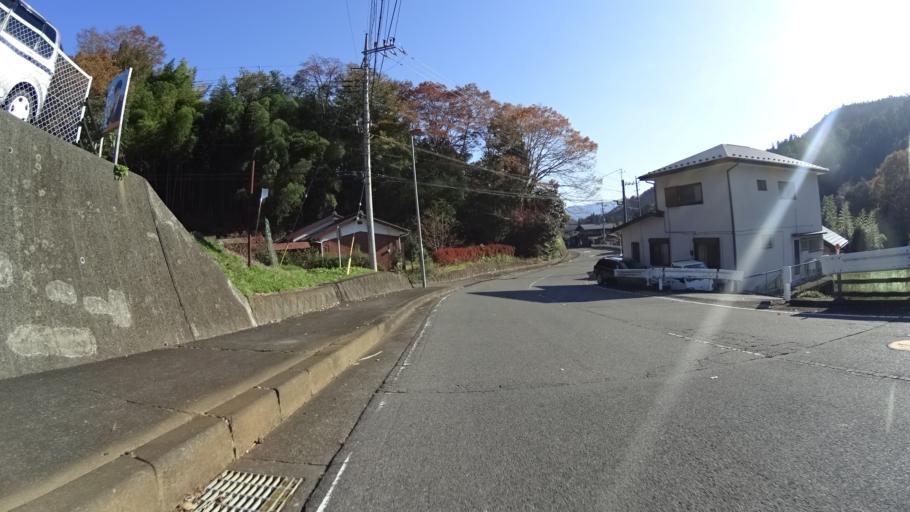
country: JP
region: Yamanashi
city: Uenohara
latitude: 35.6496
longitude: 139.1220
